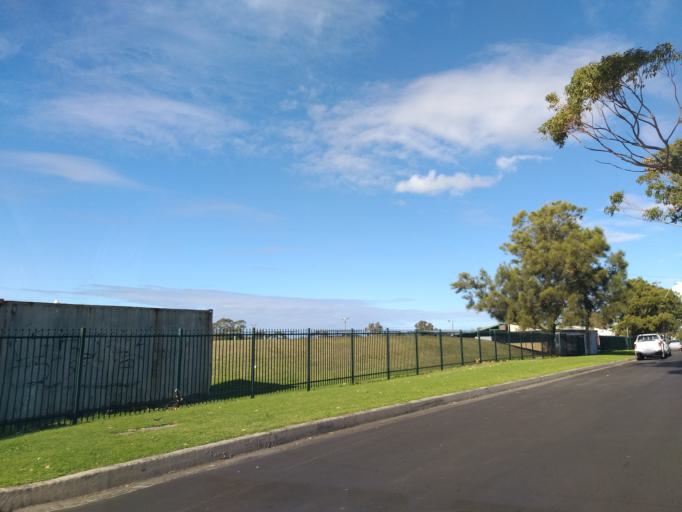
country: AU
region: New South Wales
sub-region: Wollongong
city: East Corrimal
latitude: -34.3669
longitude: 150.9169
